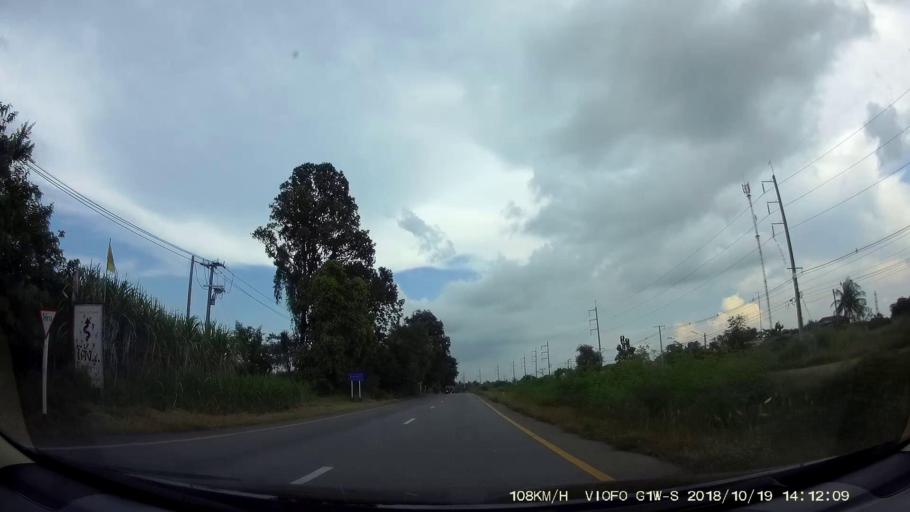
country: TH
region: Chaiyaphum
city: Khon Sawan
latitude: 15.9451
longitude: 102.1701
